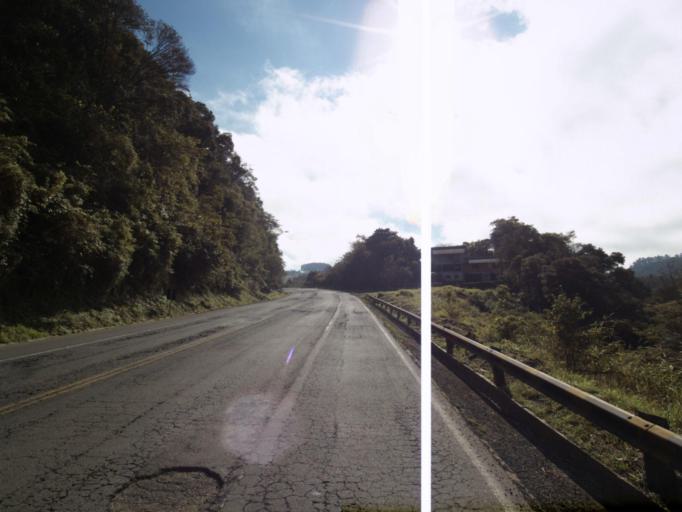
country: BR
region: Rio Grande do Sul
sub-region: Frederico Westphalen
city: Frederico Westphalen
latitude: -27.1286
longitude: -53.2123
